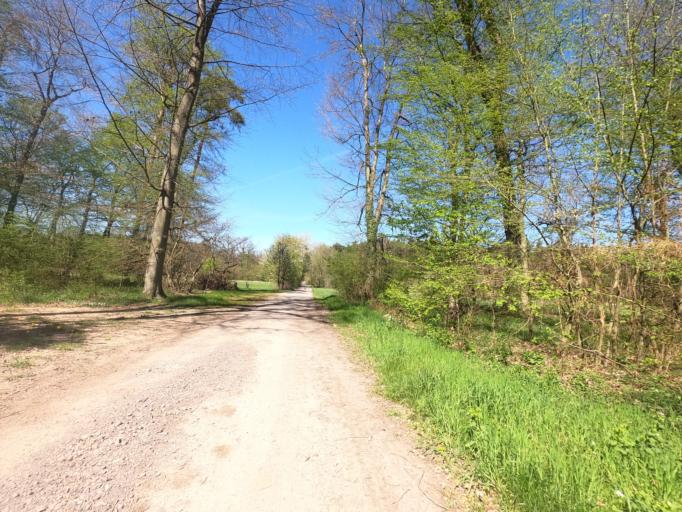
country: DE
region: Hesse
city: Morfelden-Walldorf
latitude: 49.9585
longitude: 8.5940
